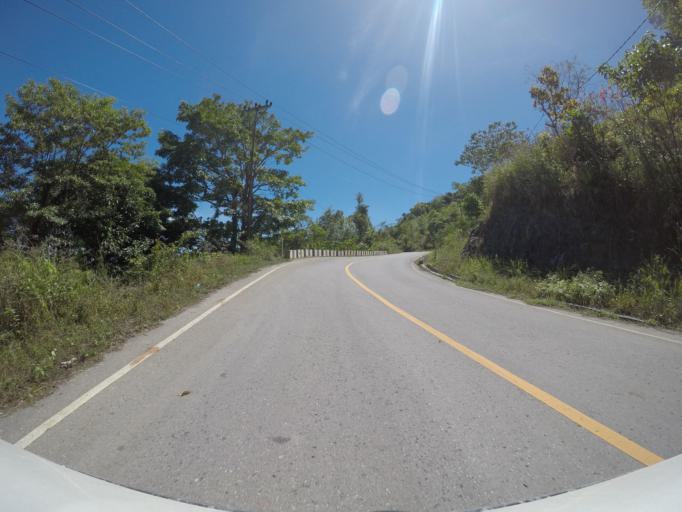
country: TL
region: Manatuto
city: Manatuto
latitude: -8.8019
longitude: 125.9692
